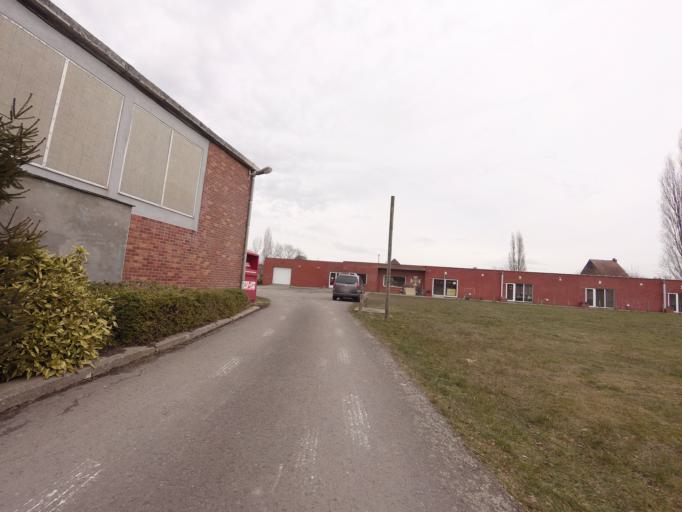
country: BE
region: Flanders
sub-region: Provincie Antwerpen
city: Boom
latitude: 51.1106
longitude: 4.3612
